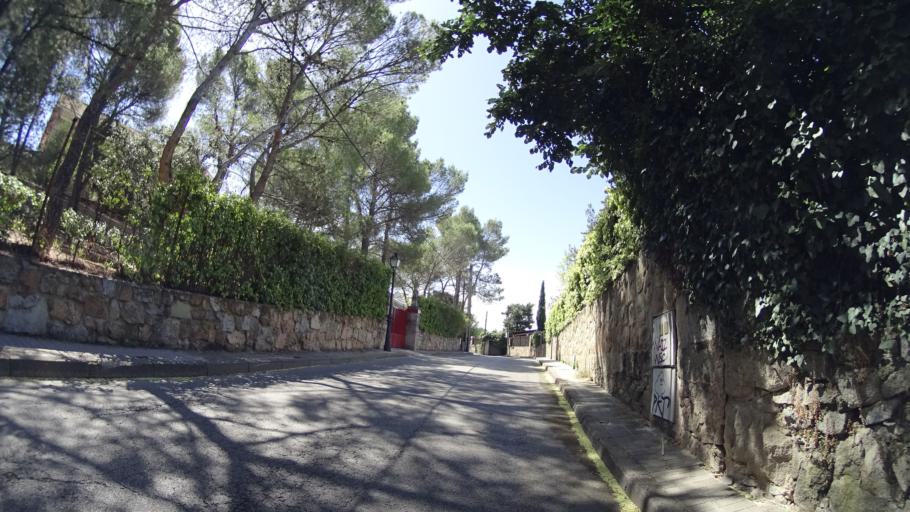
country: ES
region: Madrid
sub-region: Provincia de Madrid
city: Torrelodones
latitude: 40.5723
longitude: -3.9528
